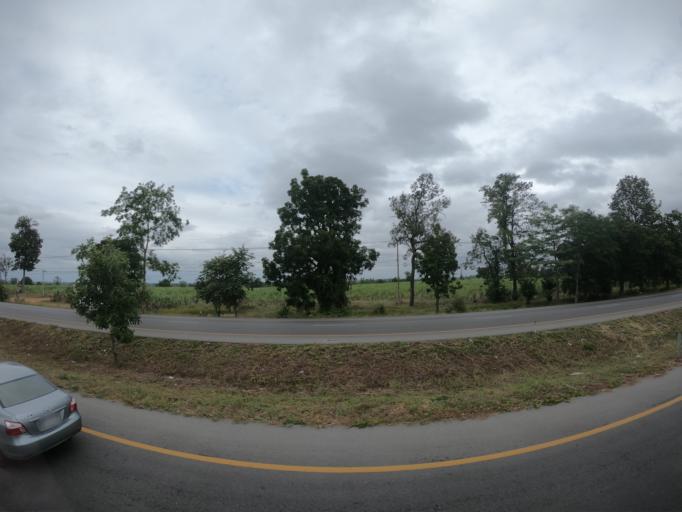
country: TH
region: Khon Kaen
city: Ban Phai
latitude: 16.0443
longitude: 102.8505
